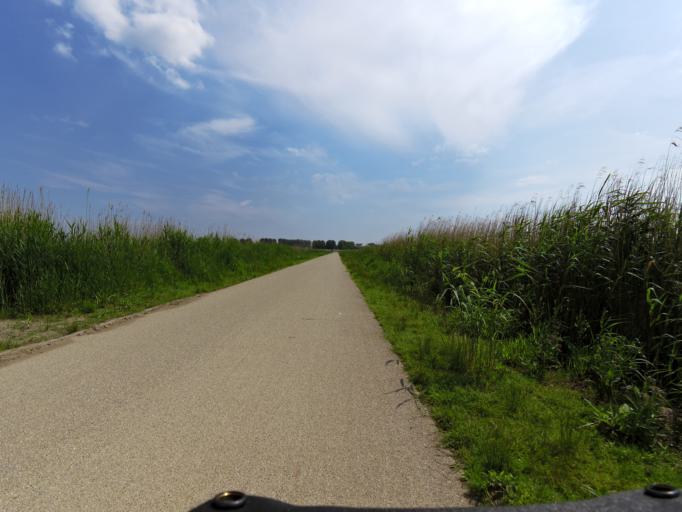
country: NL
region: North Brabant
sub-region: Gemeente Woudrichem
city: Woudrichem
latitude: 51.8091
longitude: 5.0439
